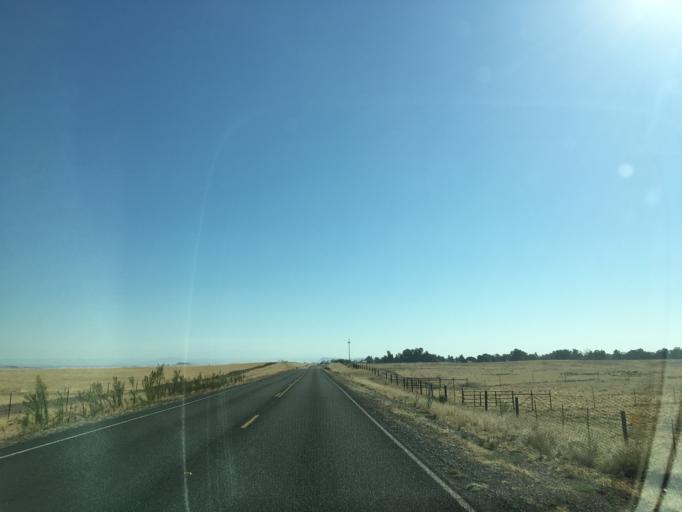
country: US
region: California
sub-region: Madera County
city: Bonadelle Ranchos-Madera Ranchos
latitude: 37.0103
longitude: -119.9038
